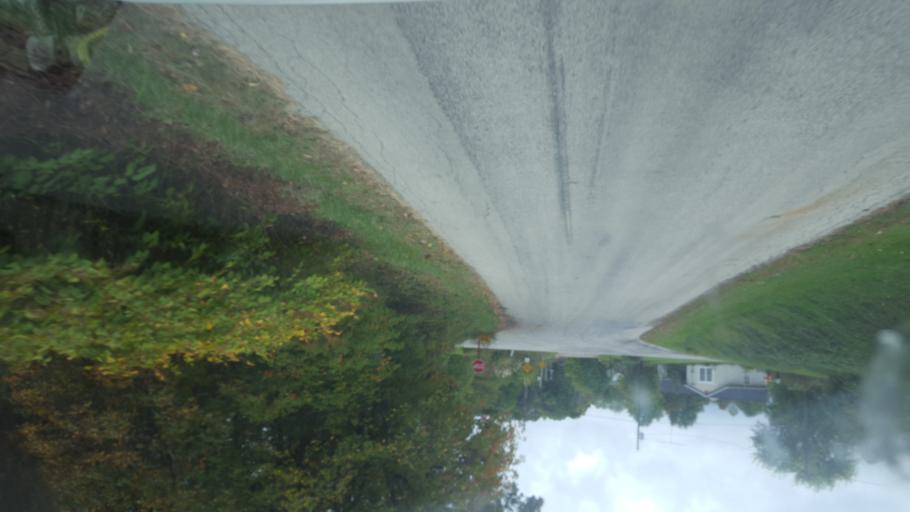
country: US
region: Ohio
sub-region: Wayne County
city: Shreve
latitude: 40.5794
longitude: -82.1094
